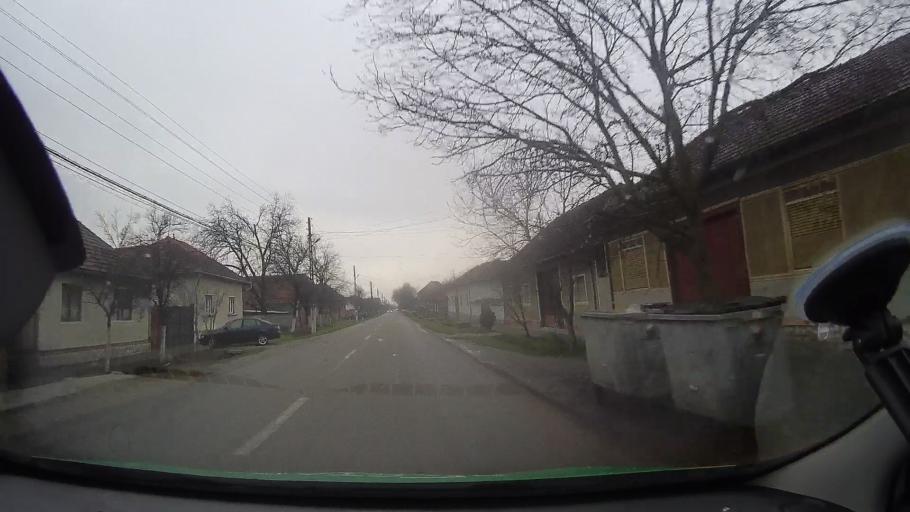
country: RO
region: Arad
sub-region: Comuna Dezna
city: Dezna
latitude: 46.4058
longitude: 22.2333
